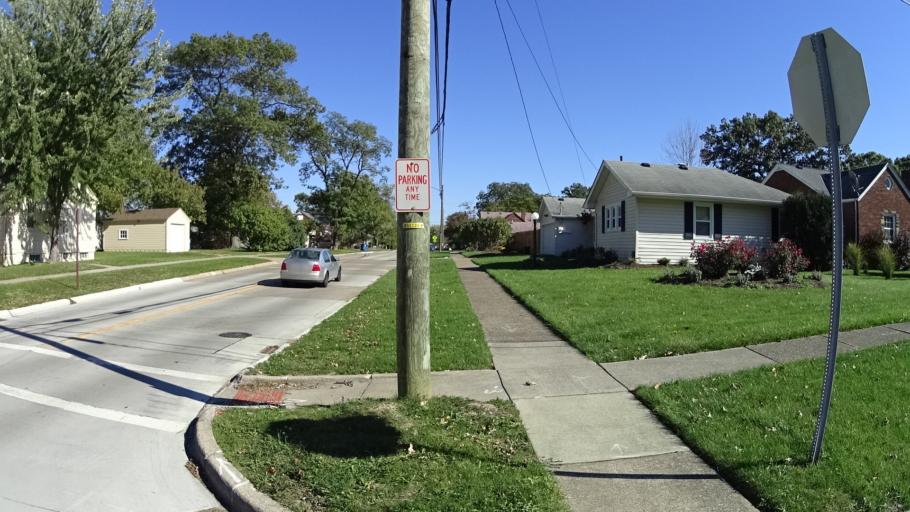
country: US
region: Ohio
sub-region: Lorain County
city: Lorain
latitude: 41.4399
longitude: -82.1730
